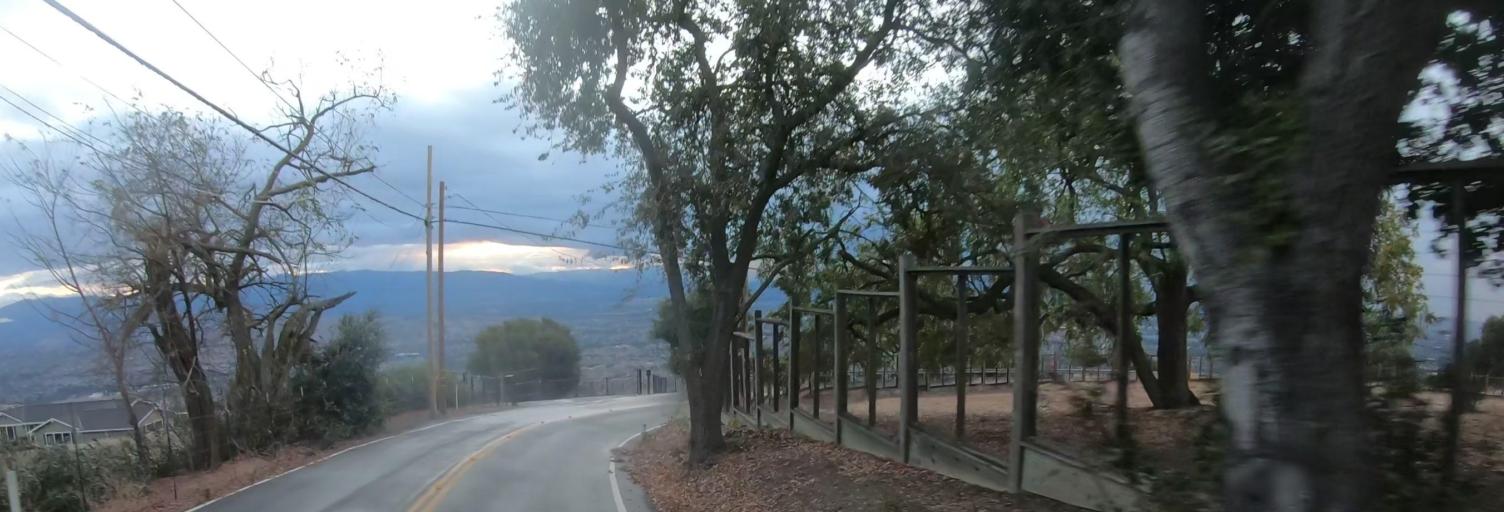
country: US
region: California
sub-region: Santa Clara County
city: East Foothills
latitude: 37.3282
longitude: -121.7470
